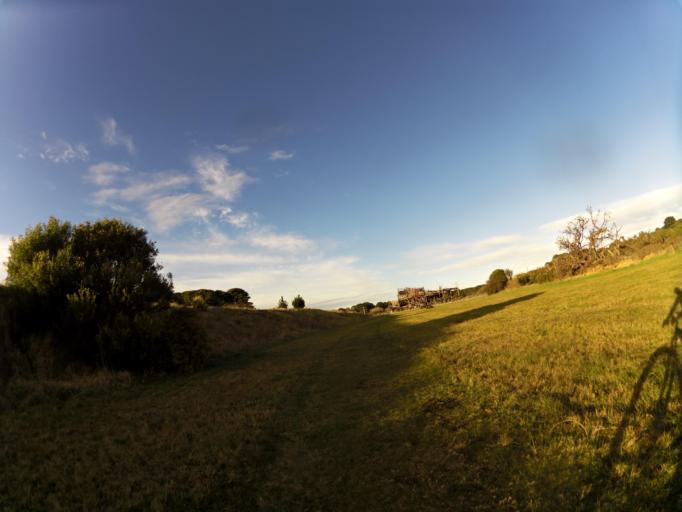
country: AU
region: Victoria
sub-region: Bass Coast
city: North Wonthaggi
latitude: -38.6033
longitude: 145.5739
